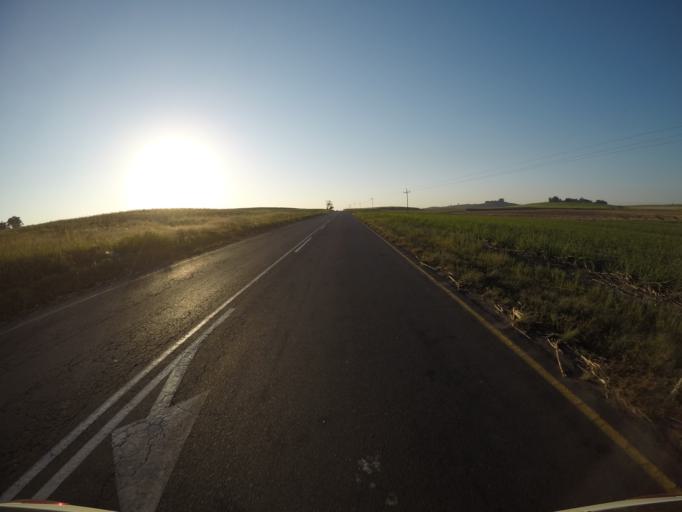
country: ZA
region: KwaZulu-Natal
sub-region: uThungulu District Municipality
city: eSikhawini
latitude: -28.9486
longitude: 31.7202
